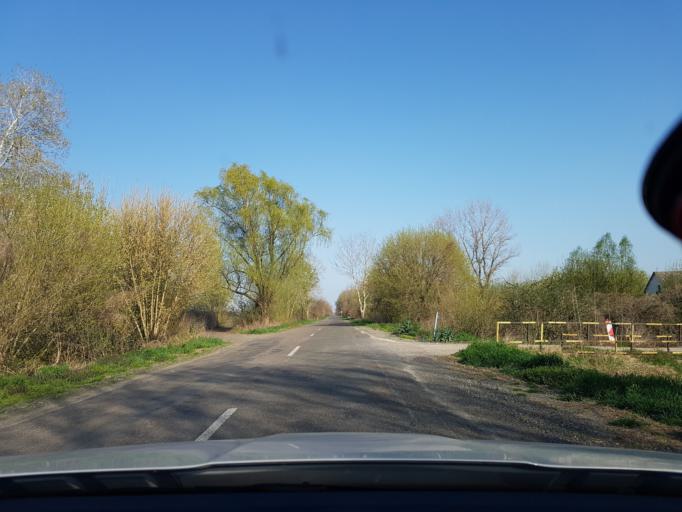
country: HU
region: Tolna
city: Ocseny
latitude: 46.3379
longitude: 18.7799
